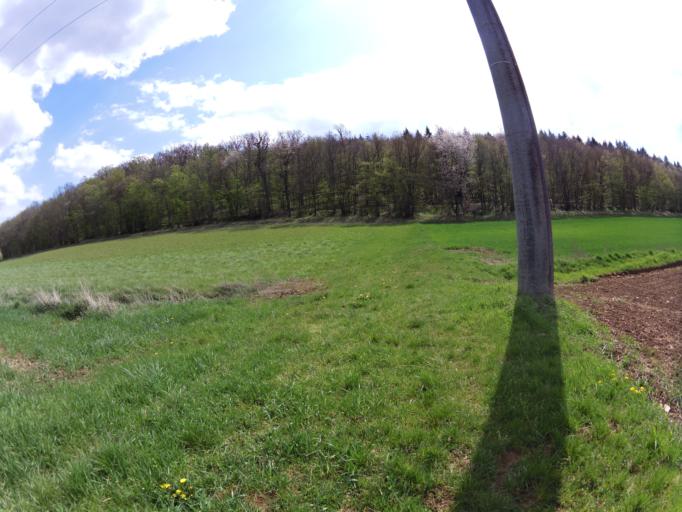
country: DE
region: Bavaria
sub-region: Regierungsbezirk Unterfranken
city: Greussenheim
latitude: 49.7947
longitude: 9.7763
